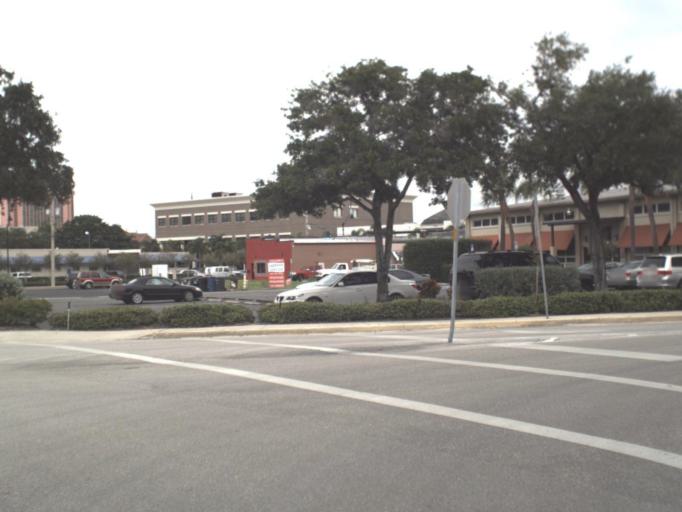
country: US
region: Florida
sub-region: Lee County
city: North Fort Myers
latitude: 26.6397
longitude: -81.8686
